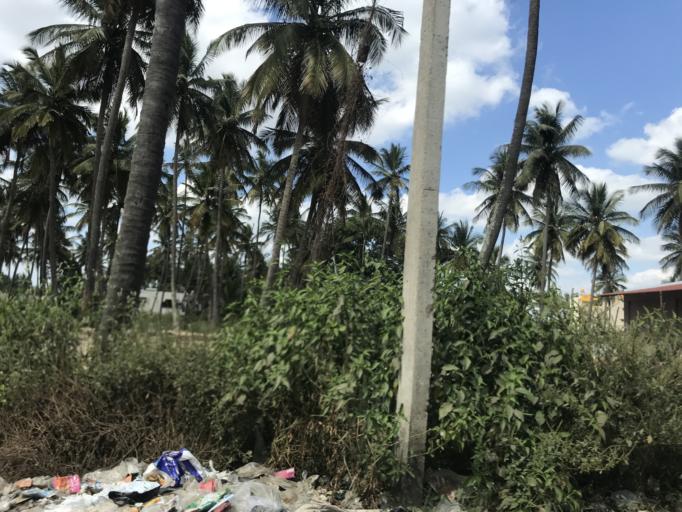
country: IN
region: Karnataka
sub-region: Mandya
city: Krishnarajpet
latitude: 12.7606
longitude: 76.4232
